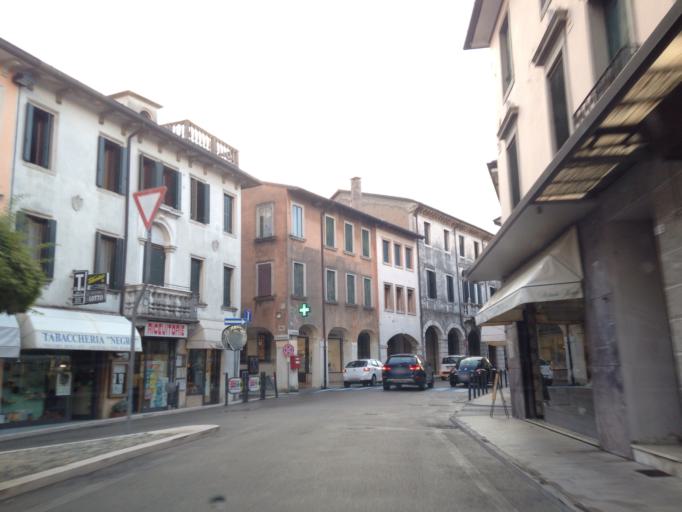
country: IT
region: Friuli Venezia Giulia
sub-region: Provincia di Pordenone
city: Sacile
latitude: 45.9537
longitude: 12.5009
